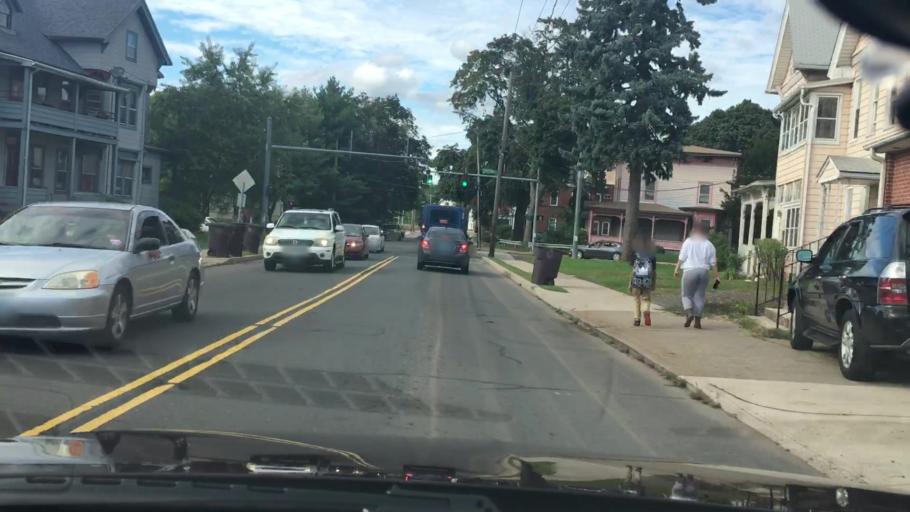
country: US
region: Connecticut
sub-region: Hartford County
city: New Britain
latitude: 41.6660
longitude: -72.7712
